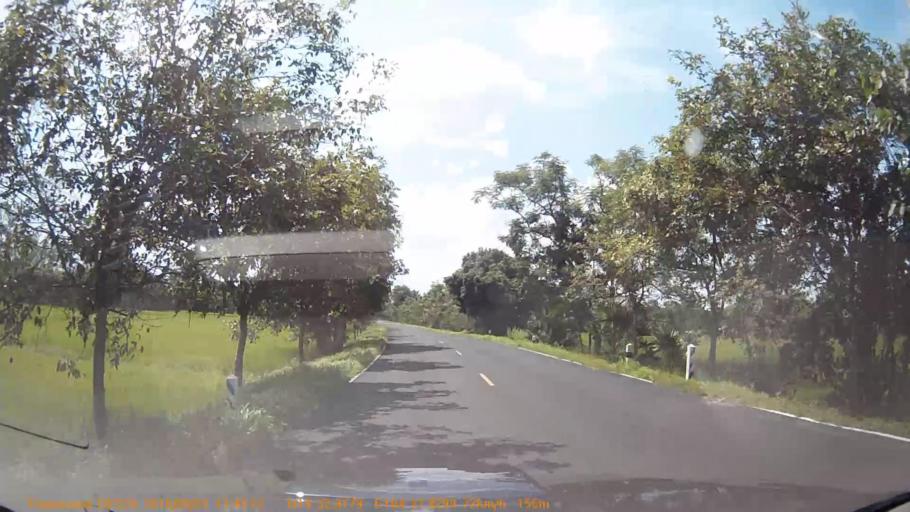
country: TH
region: Sisaket
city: Khun Han
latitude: 14.5471
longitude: 104.4650
